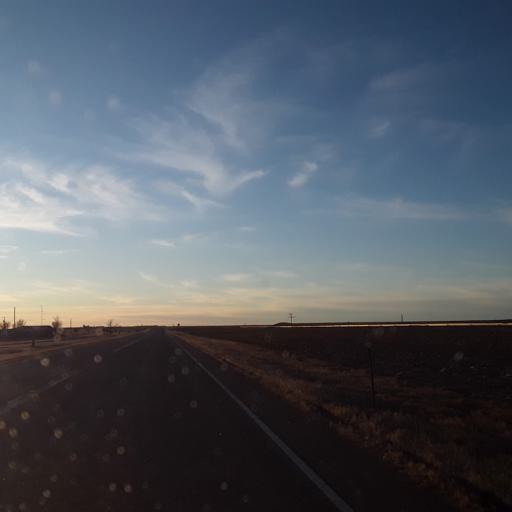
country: US
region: Colorado
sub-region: Cheyenne County
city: Cheyenne Wells
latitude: 38.8134
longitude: -102.3810
